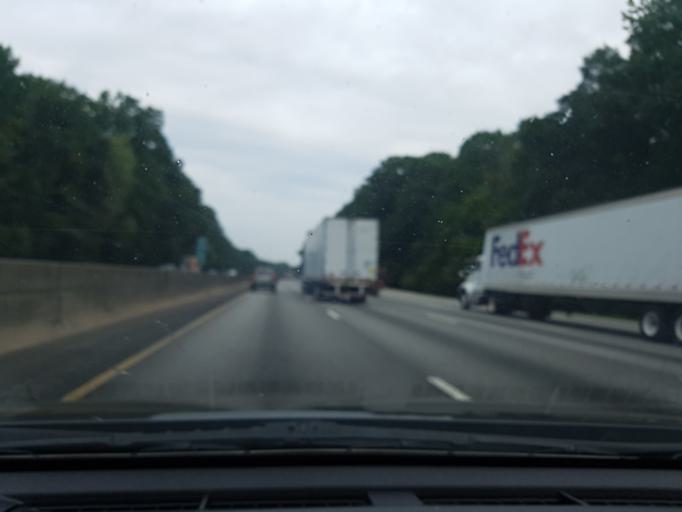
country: US
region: Georgia
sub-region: DeKalb County
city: Gresham Park
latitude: 33.6858
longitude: -84.3075
